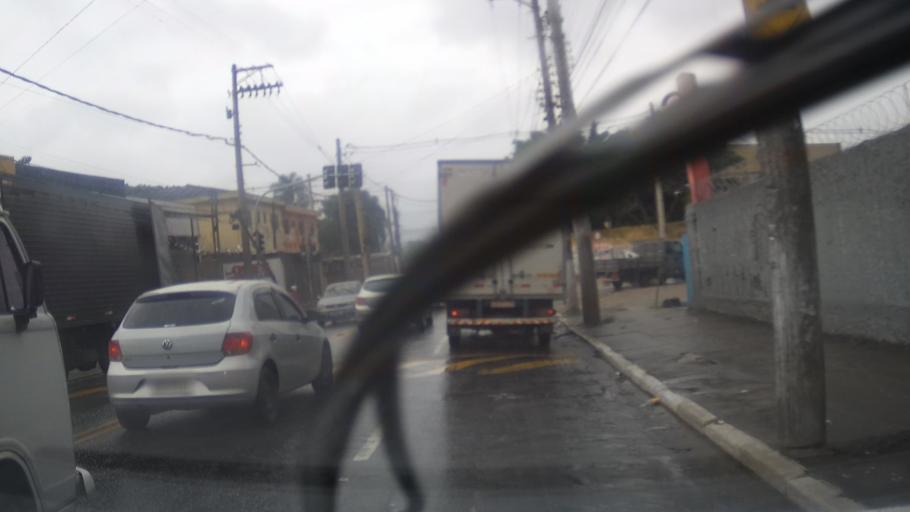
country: BR
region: Sao Paulo
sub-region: Guarulhos
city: Guarulhos
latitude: -23.4361
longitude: -46.5059
